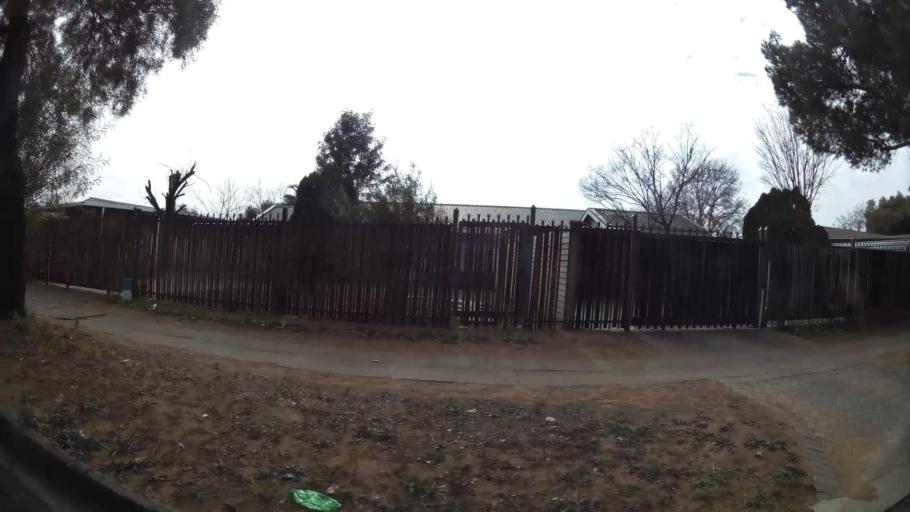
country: ZA
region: Orange Free State
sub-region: Mangaung Metropolitan Municipality
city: Bloemfontein
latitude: -29.1299
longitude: 26.1928
